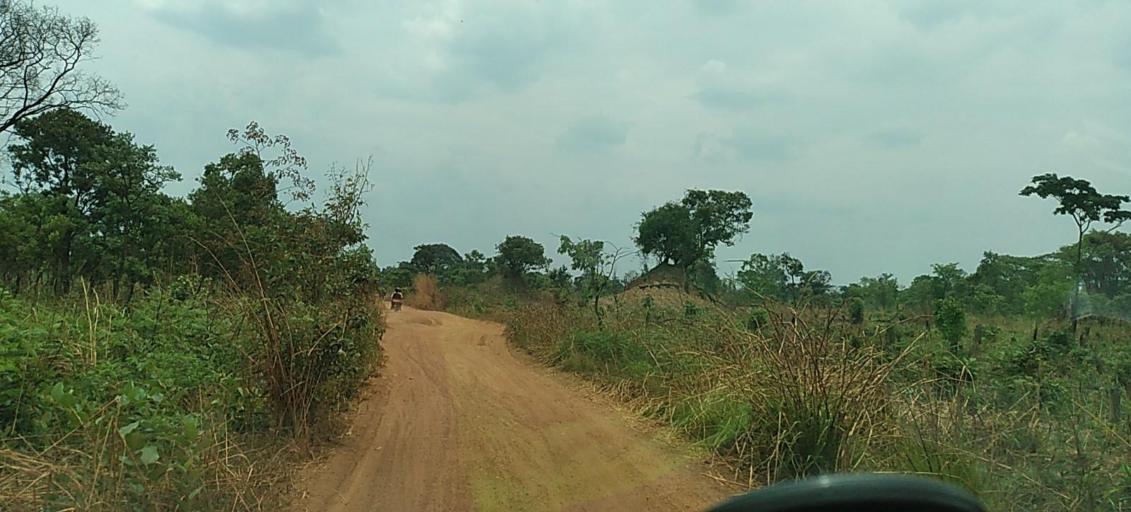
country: ZM
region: North-Western
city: Kansanshi
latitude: -12.0685
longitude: 26.3535
